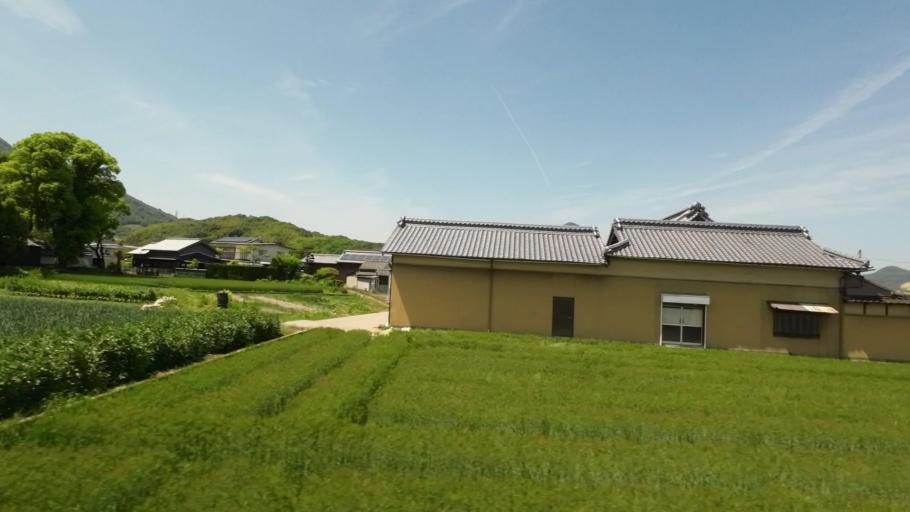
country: JP
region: Kagawa
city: Marugame
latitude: 34.2255
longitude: 133.7918
